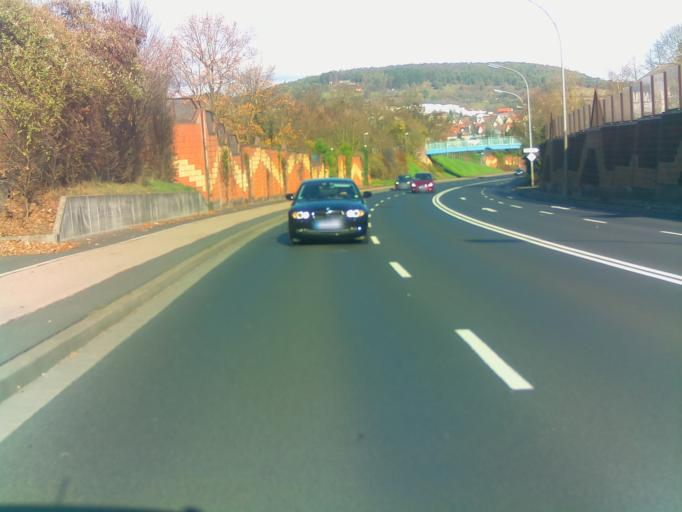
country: DE
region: Bavaria
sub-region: Regierungsbezirk Unterfranken
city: Bad Kissingen
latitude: 50.1981
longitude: 10.0857
